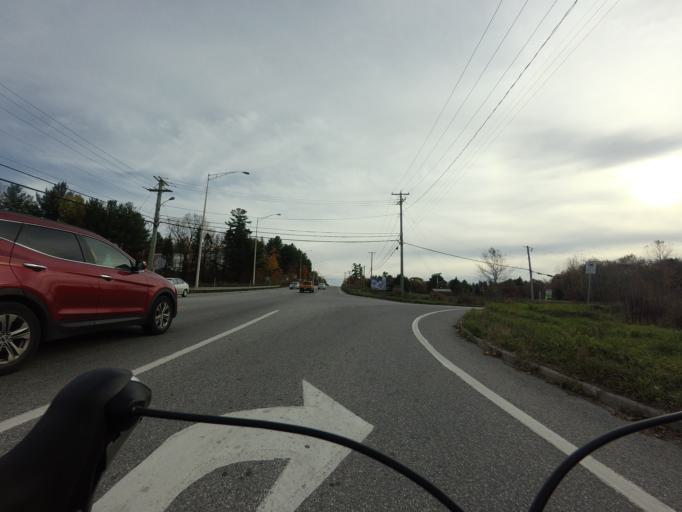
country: CA
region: Quebec
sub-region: Outaouais
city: Wakefield
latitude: 45.5664
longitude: -75.7824
